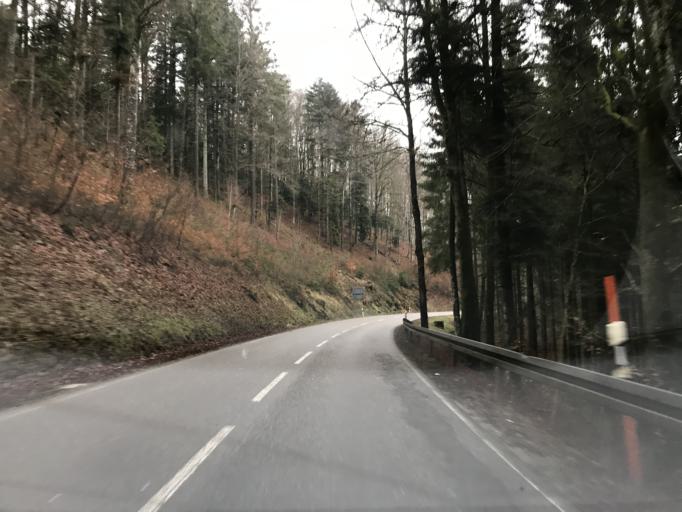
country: DE
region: Baden-Wuerttemberg
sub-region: Freiburg Region
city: Rickenbach
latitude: 47.6149
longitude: 7.9756
